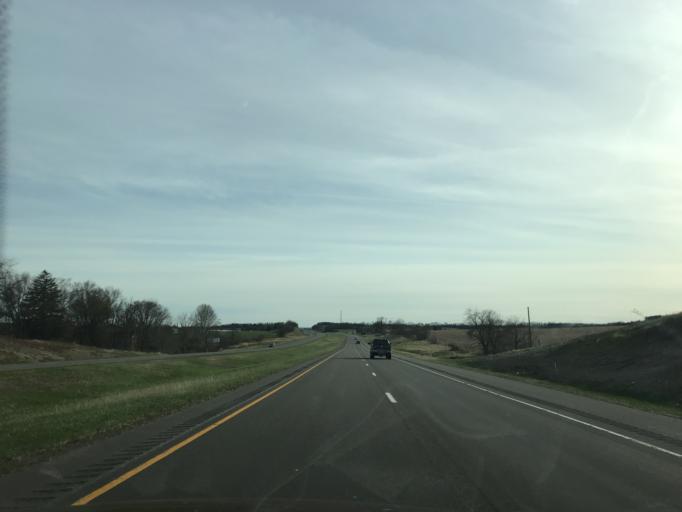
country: US
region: Pennsylvania
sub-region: Northumberland County
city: Watsontown
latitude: 41.0892
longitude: -76.8158
